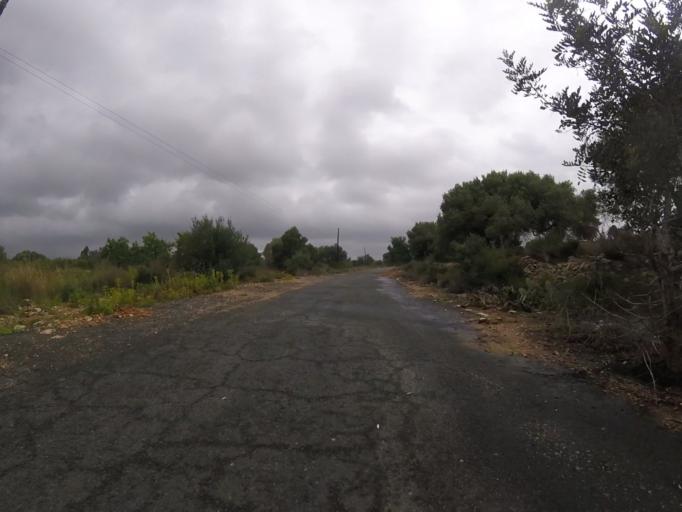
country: ES
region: Valencia
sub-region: Provincia de Castello
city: Alcala de Xivert
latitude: 40.2800
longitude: 0.2257
